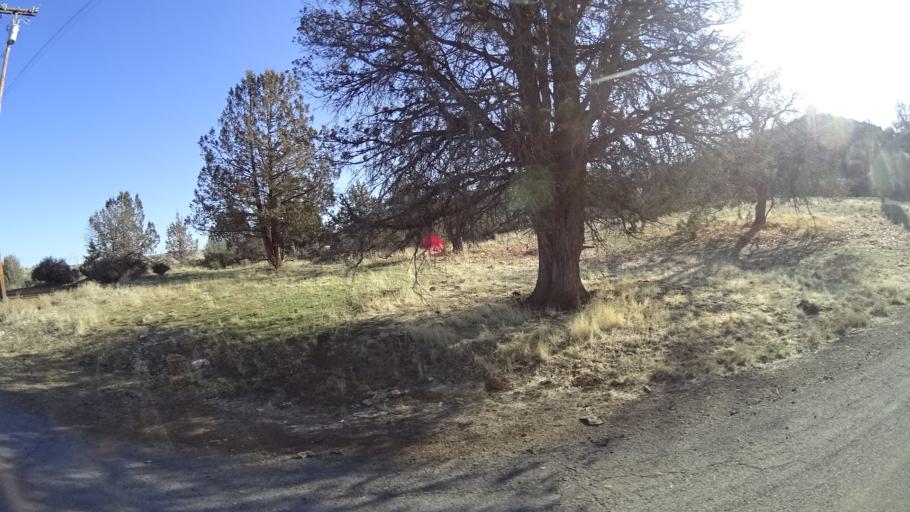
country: US
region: California
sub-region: Siskiyou County
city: Montague
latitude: 41.8908
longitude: -122.4892
